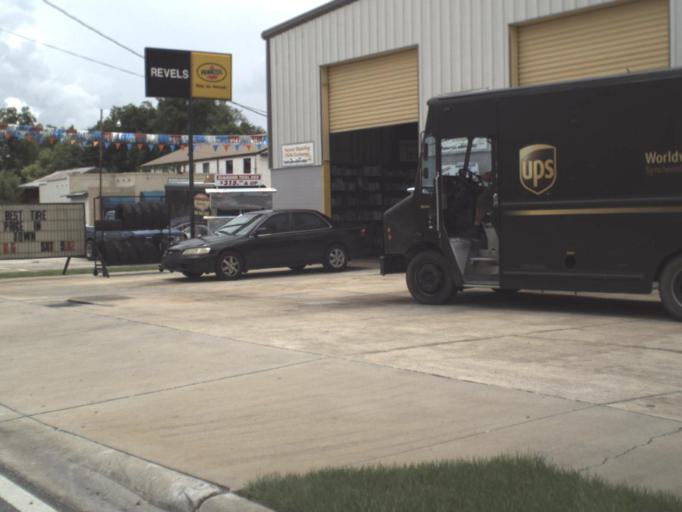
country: US
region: Florida
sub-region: Bradford County
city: Starke
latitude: 29.9435
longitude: -82.1106
